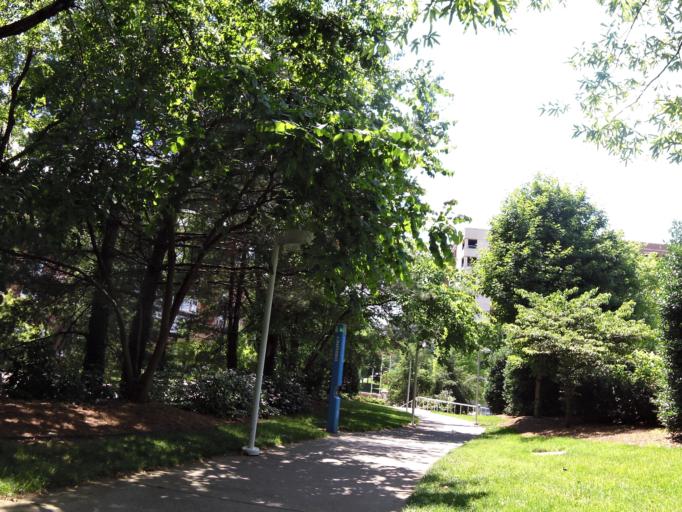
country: US
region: Tennessee
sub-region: Knox County
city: Knoxville
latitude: 35.9596
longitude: -83.9239
